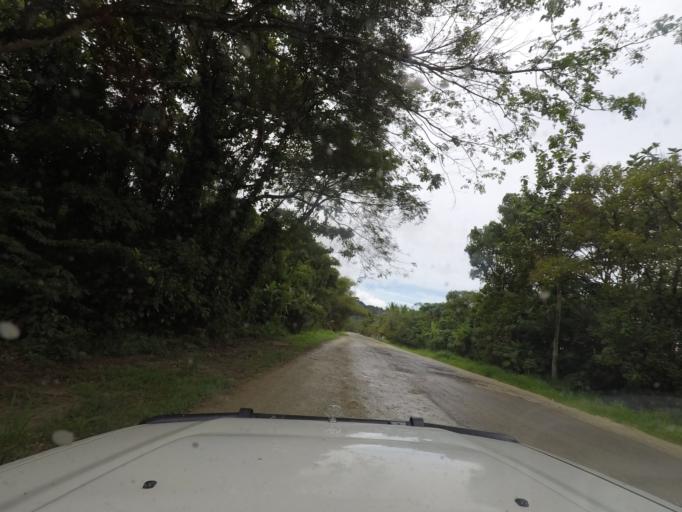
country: PG
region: Eastern Highlands
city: Goroka
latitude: -5.6286
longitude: 145.4804
